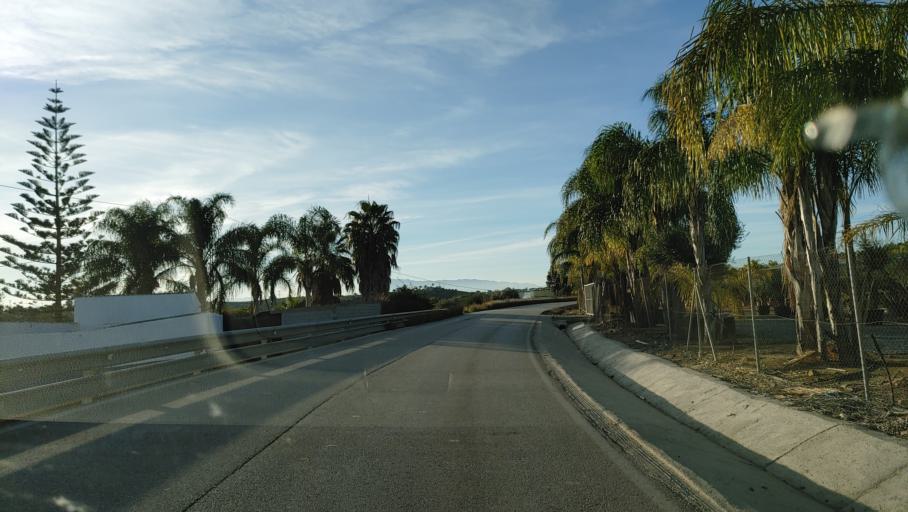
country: ES
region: Andalusia
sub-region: Provincia de Malaga
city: Cartama
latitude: 36.6784
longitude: -4.6269
